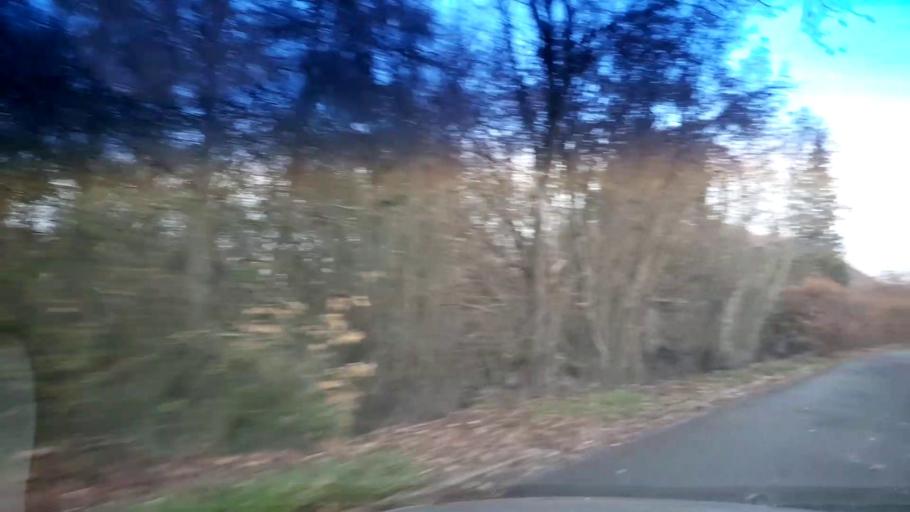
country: DE
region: Bavaria
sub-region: Upper Franconia
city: Stegaurach
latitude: 49.8618
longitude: 10.8322
